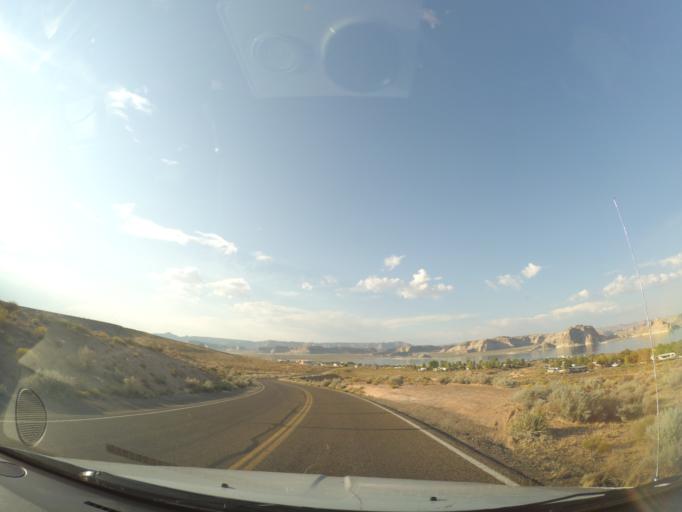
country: US
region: Arizona
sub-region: Coconino County
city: Page
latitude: 36.9962
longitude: -111.5030
